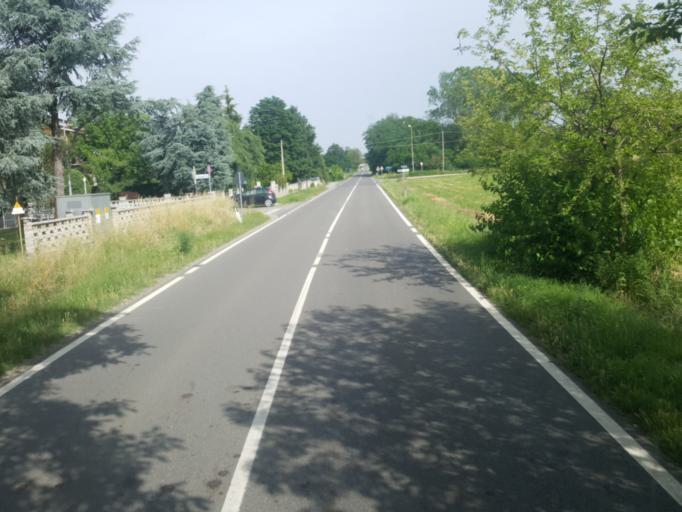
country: IT
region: Emilia-Romagna
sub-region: Provincia di Piacenza
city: Niviano
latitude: 44.9397
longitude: 9.6396
